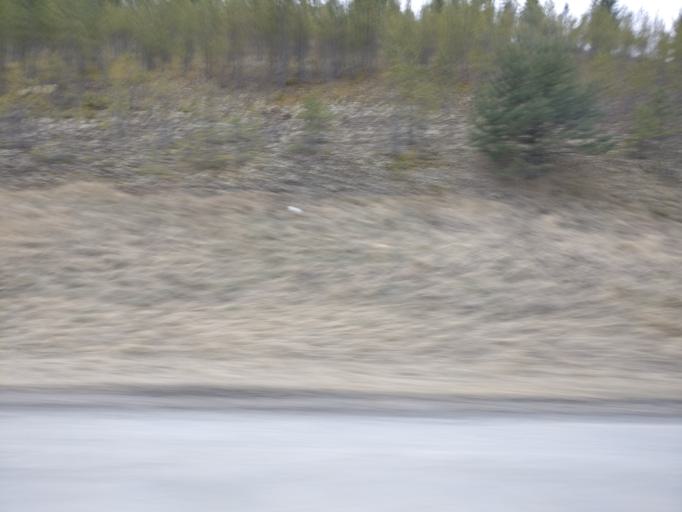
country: FI
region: Haeme
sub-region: Haemeenlinna
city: Parola
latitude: 61.0569
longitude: 24.3446
